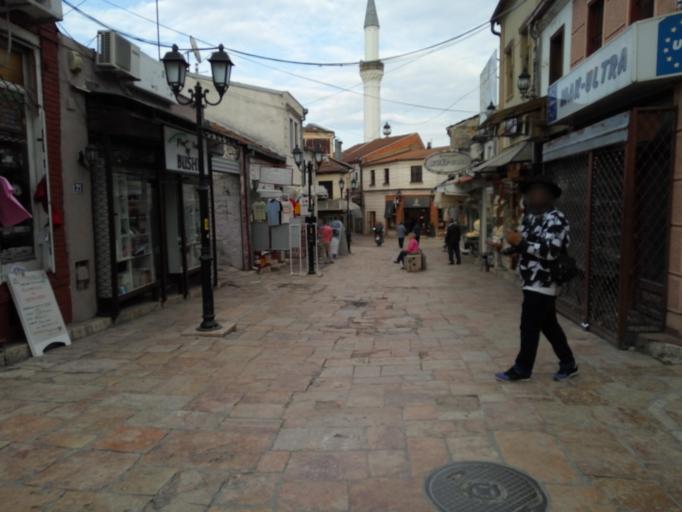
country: MK
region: Karpos
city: Skopje
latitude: 42.0008
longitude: 21.4365
